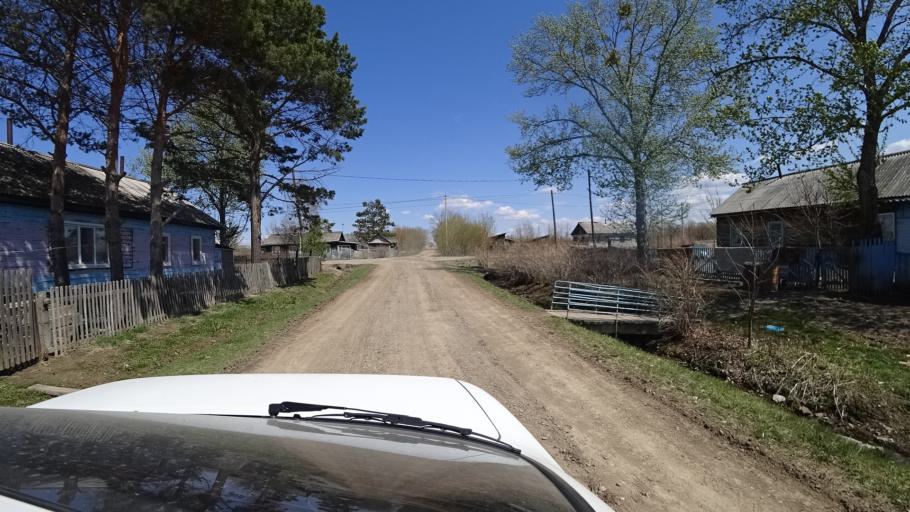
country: RU
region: Primorskiy
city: Dal'nerechensk
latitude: 45.7925
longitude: 133.7719
